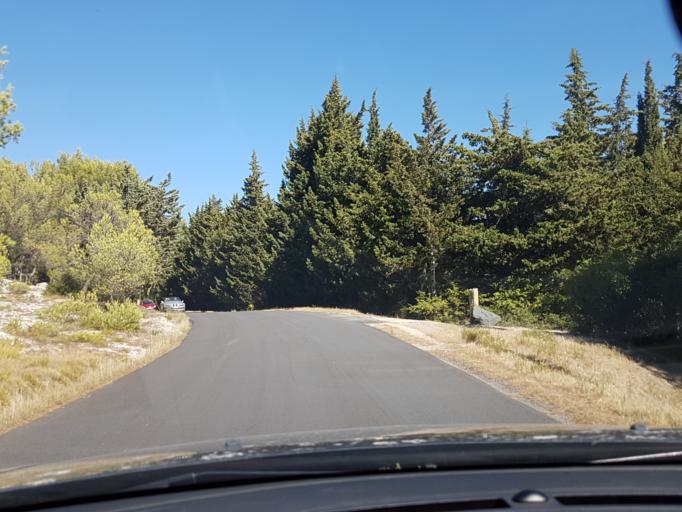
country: FR
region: Provence-Alpes-Cote d'Azur
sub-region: Departement des Bouches-du-Rhone
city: Eygalieres
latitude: 43.7640
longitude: 4.9724
